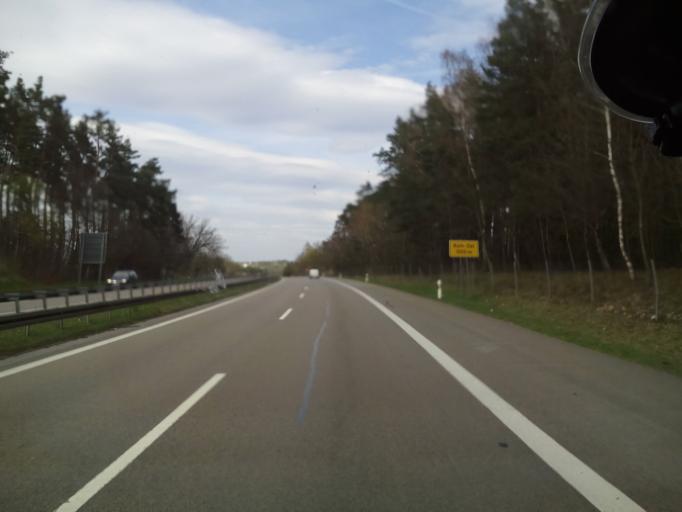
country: DE
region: Bavaria
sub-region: Regierungsbezirk Mittelfranken
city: Roth
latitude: 49.2362
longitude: 11.1019
